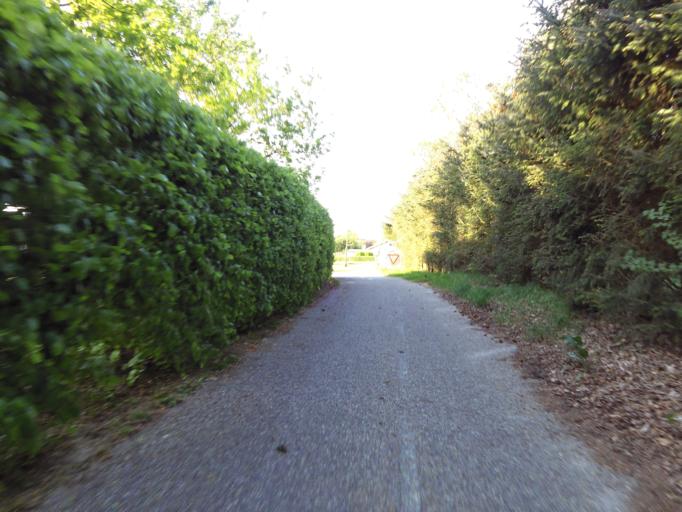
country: DK
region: South Denmark
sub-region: Esbjerg Kommune
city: Ribe
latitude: 55.2850
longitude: 8.7318
